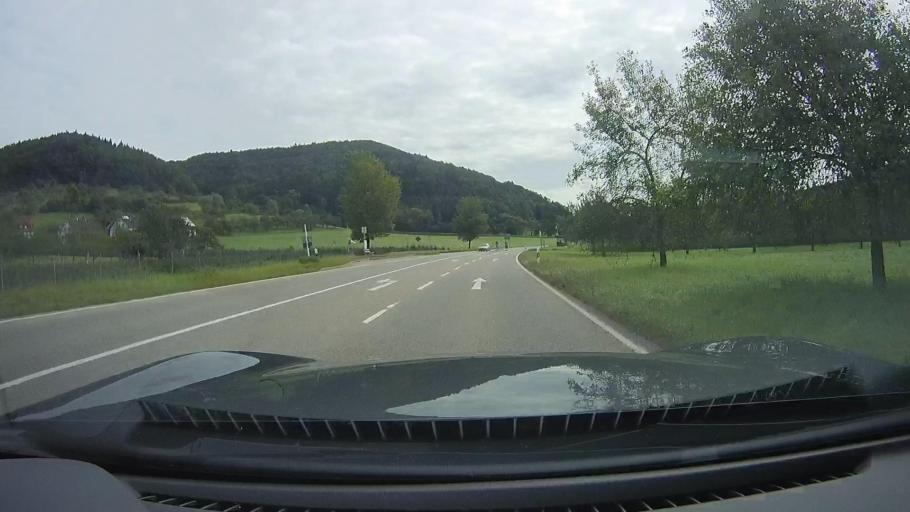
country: DE
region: Baden-Wuerttemberg
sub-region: Regierungsbezirk Stuttgart
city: Sulzbach an der Murr
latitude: 49.0168
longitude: 9.4697
